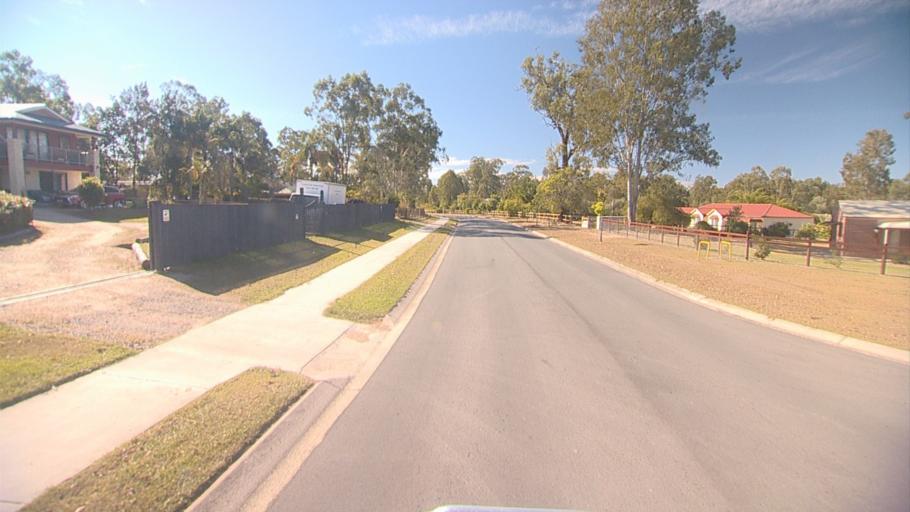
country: AU
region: Queensland
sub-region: Logan
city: North Maclean
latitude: -27.8112
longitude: 152.9618
